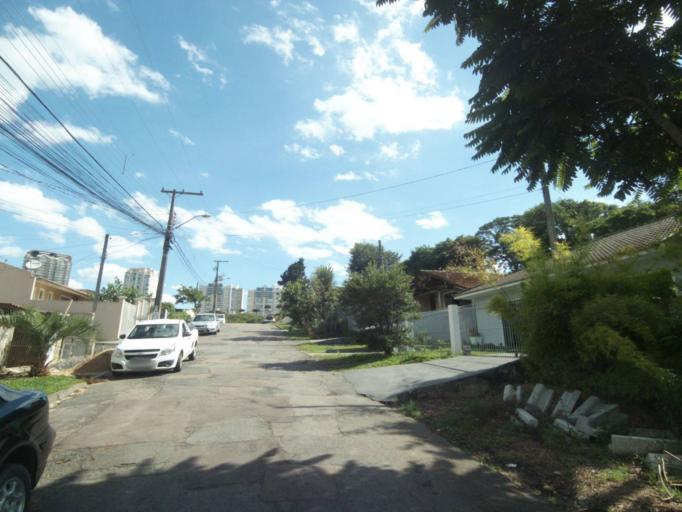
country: BR
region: Parana
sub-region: Curitiba
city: Curitiba
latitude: -25.4351
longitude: -49.3448
